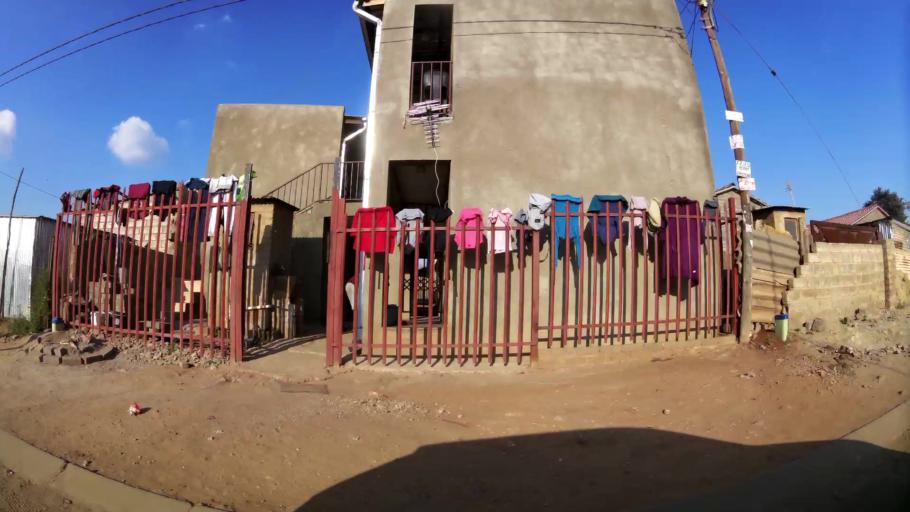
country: ZA
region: Gauteng
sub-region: Ekurhuleni Metropolitan Municipality
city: Tembisa
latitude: -25.9679
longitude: 28.2147
